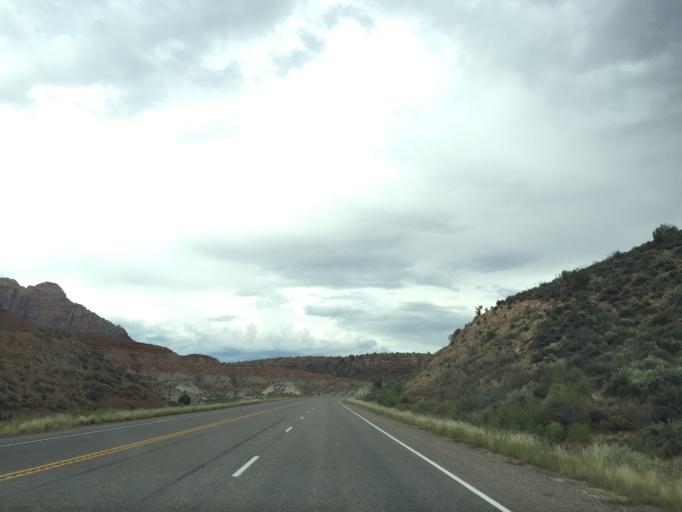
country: US
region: Utah
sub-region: Washington County
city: Hildale
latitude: 37.1706
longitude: -113.0736
